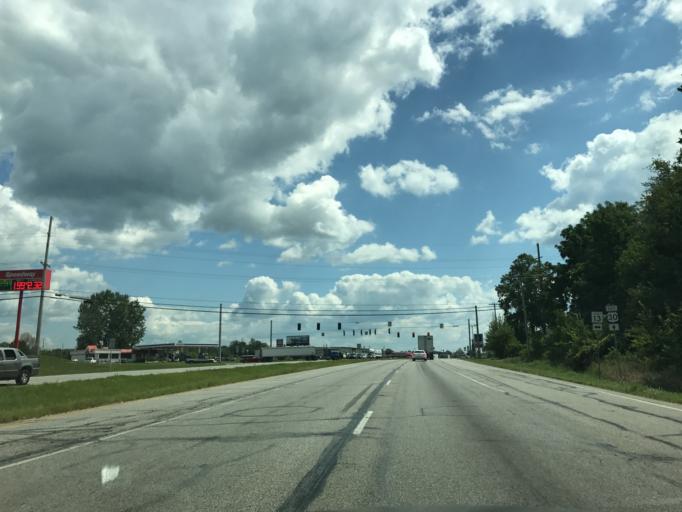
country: US
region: Indiana
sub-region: Kosciusko County
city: Pierceton
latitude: 41.2048
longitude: -85.7071
